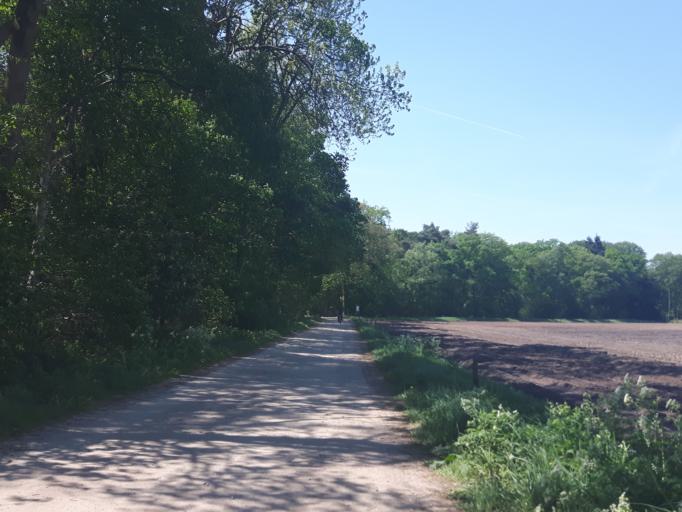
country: NL
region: Overijssel
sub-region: Gemeente Enschede
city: Enschede
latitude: 52.1570
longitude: 6.8817
